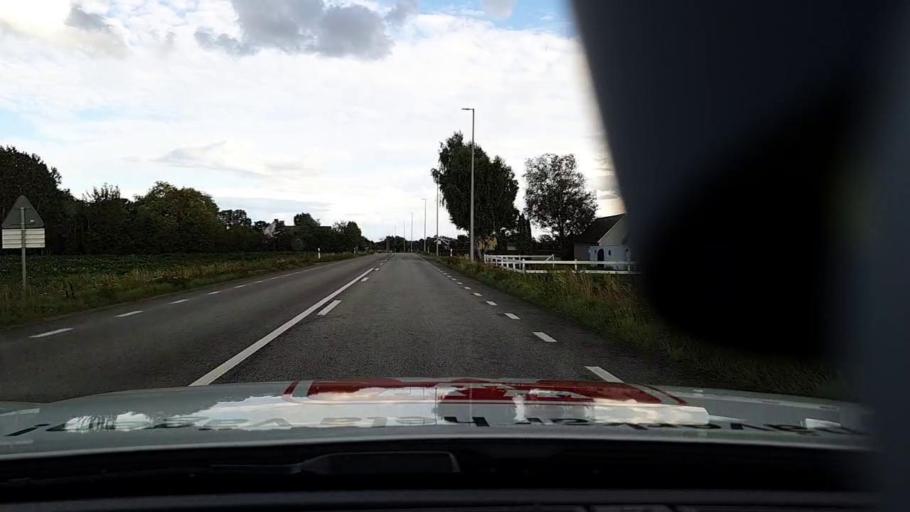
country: SE
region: Blekinge
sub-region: Solvesborgs Kommun
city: Soelvesborg
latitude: 56.0503
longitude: 14.6531
